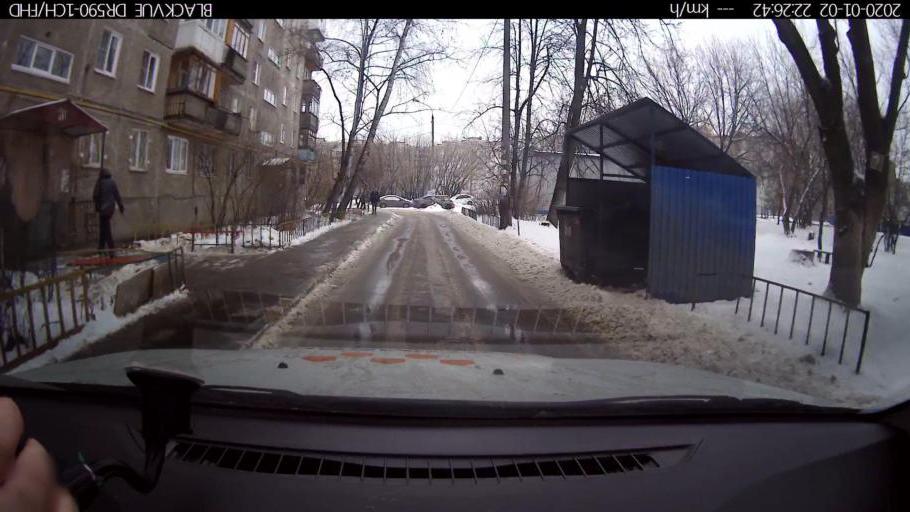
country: RU
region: Nizjnij Novgorod
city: Nizhniy Novgorod
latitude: 56.3235
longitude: 43.9352
